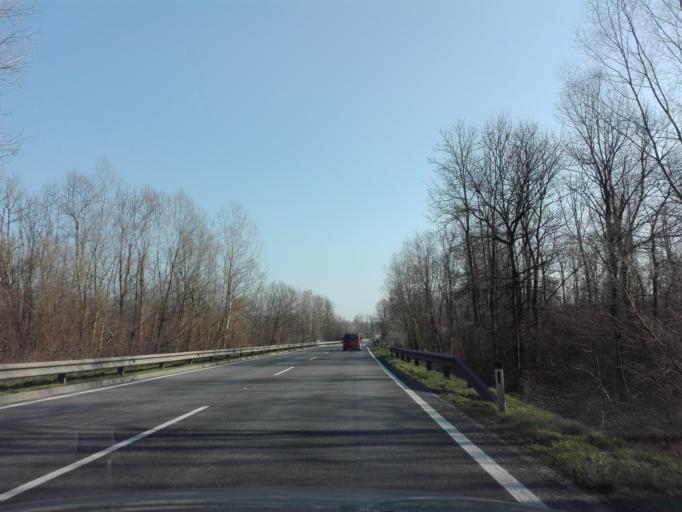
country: AT
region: Upper Austria
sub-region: Politischer Bezirk Linz-Land
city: Traun
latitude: 48.2139
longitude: 14.2367
